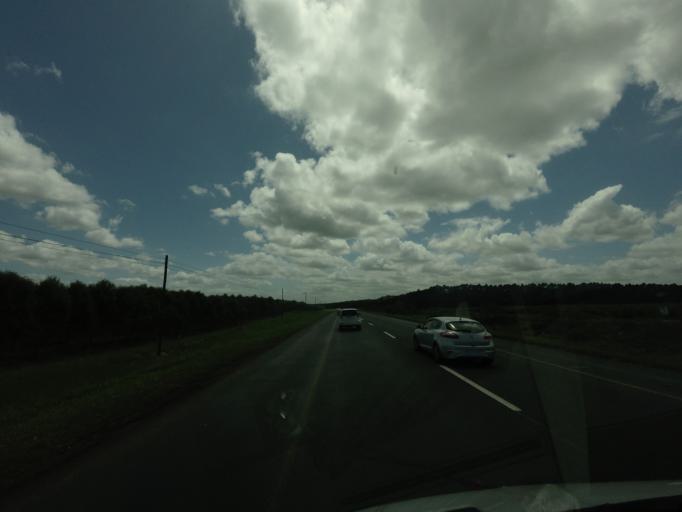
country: ZA
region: KwaZulu-Natal
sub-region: uThungulu District Municipality
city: KwaMbonambi
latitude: -28.5708
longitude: 32.1102
